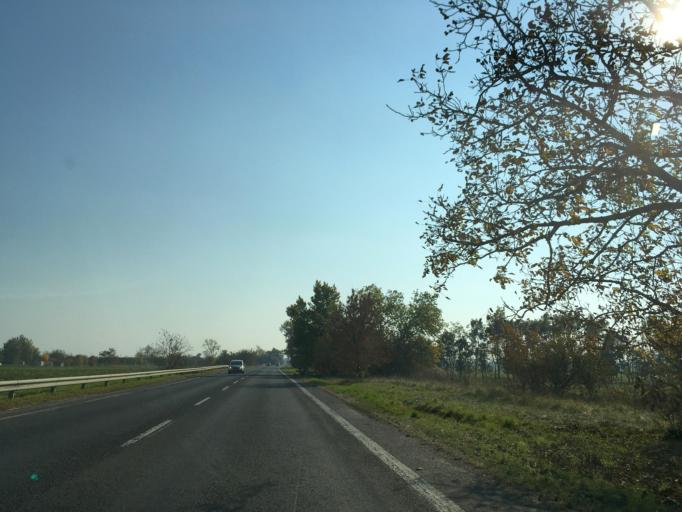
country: SK
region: Trnavsky
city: Samorin
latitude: 48.0458
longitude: 17.2950
